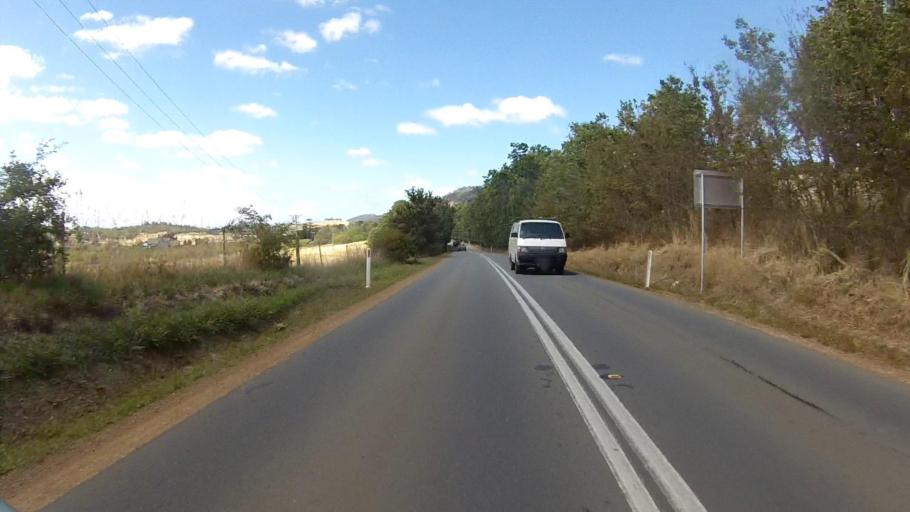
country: AU
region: Tasmania
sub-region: Clarence
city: Cambridge
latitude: -42.8055
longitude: 147.4234
